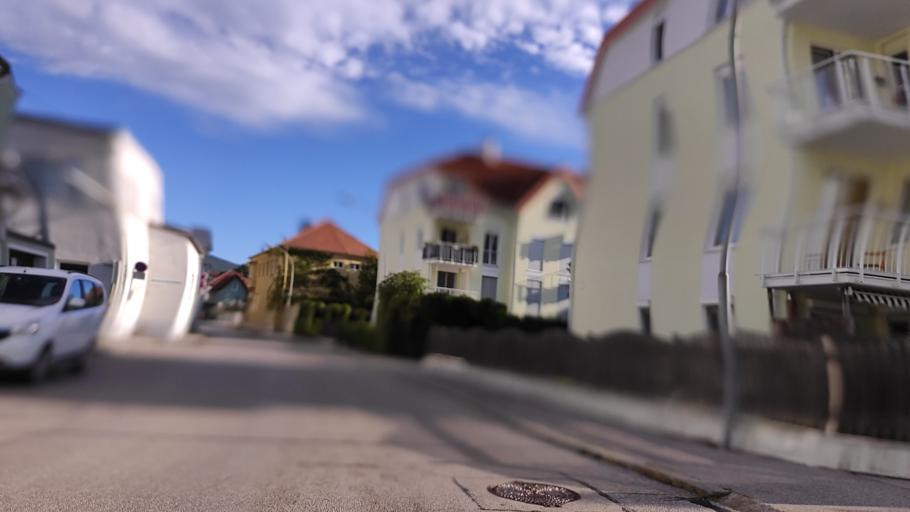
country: AT
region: Lower Austria
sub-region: Politischer Bezirk Baden
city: Pfaffstatten
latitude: 48.0072
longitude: 16.2508
